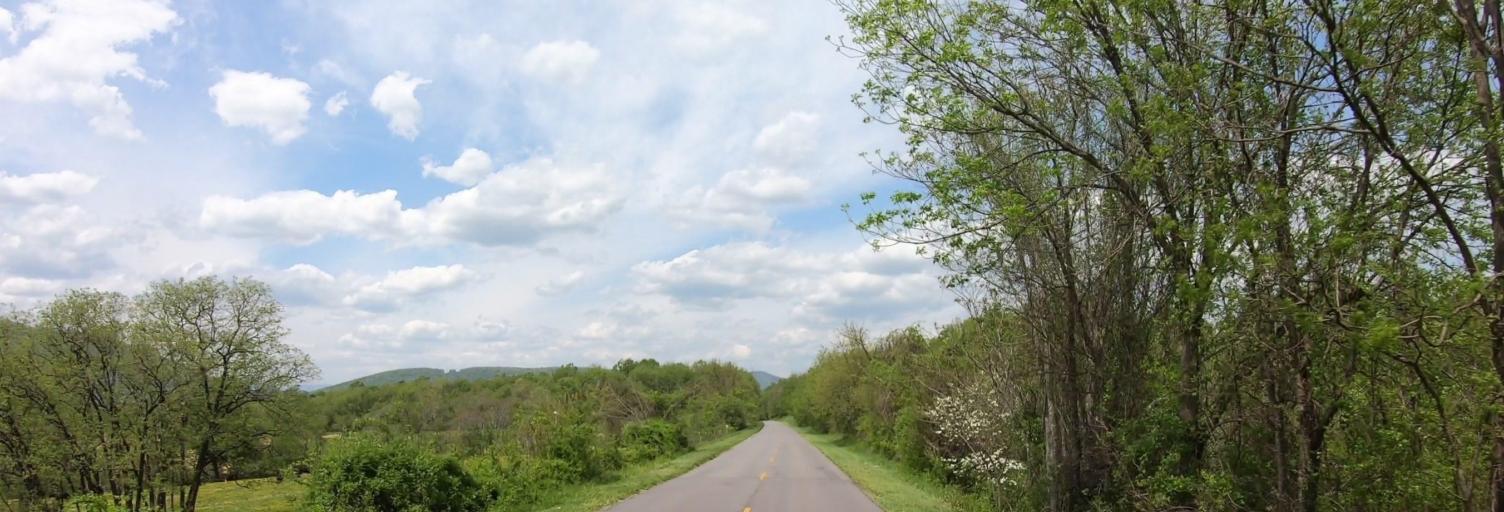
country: US
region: Virginia
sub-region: Botetourt County
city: Laymantown
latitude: 37.3166
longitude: -79.8579
